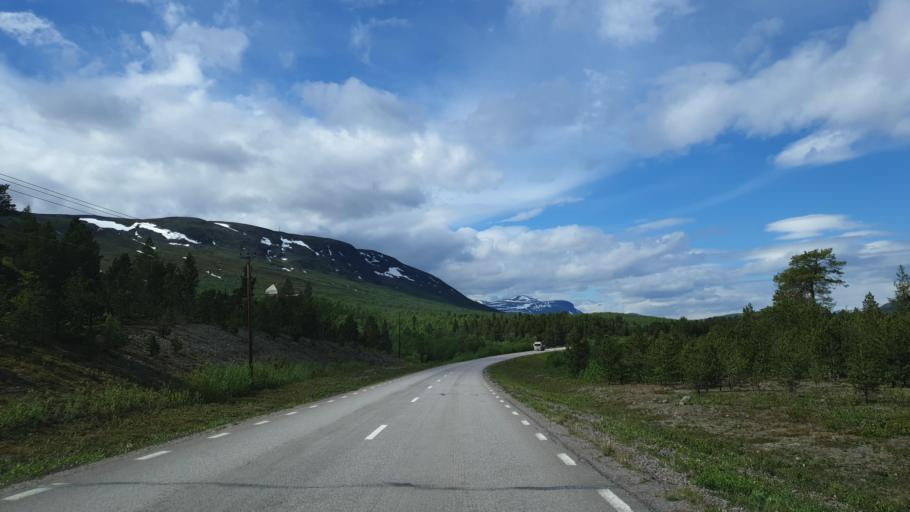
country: SE
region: Norrbotten
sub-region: Kiruna Kommun
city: Kiruna
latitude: 68.2182
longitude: 19.7251
